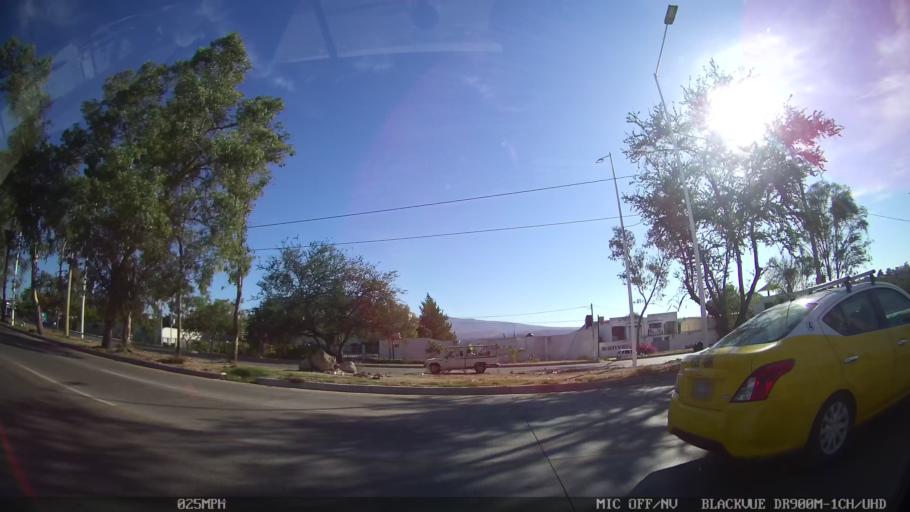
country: MX
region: Jalisco
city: Tlaquepaque
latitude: 20.6953
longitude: -103.2728
